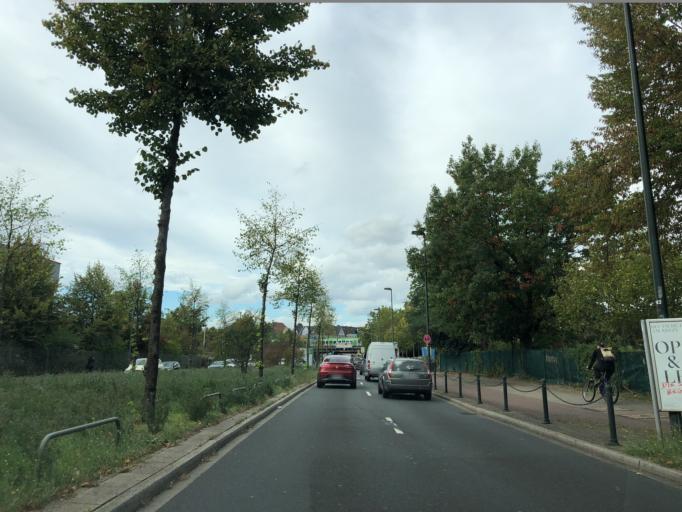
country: DE
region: North Rhine-Westphalia
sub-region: Regierungsbezirk Dusseldorf
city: Dusseldorf
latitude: 51.2060
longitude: 6.8099
